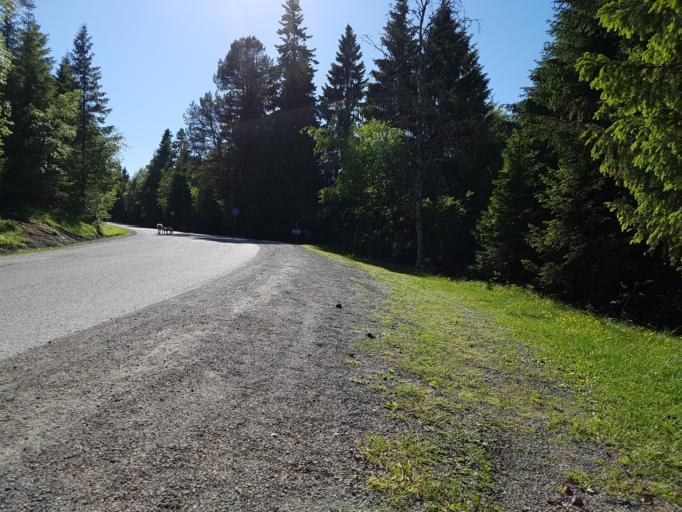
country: NO
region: Sor-Trondelag
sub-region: Trondheim
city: Trondheim
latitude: 63.4170
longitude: 10.3152
